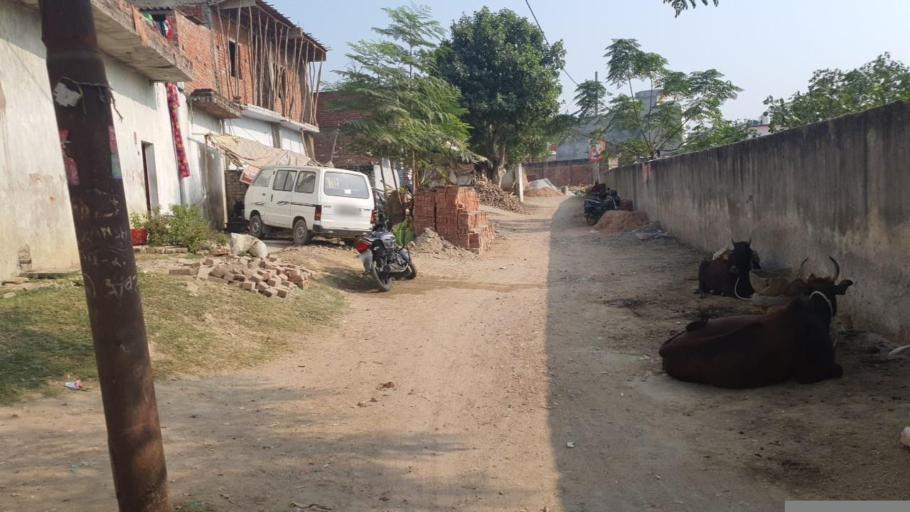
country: IN
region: Uttar Pradesh
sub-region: Lucknow District
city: Lucknow
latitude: 26.7975
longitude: 81.0070
